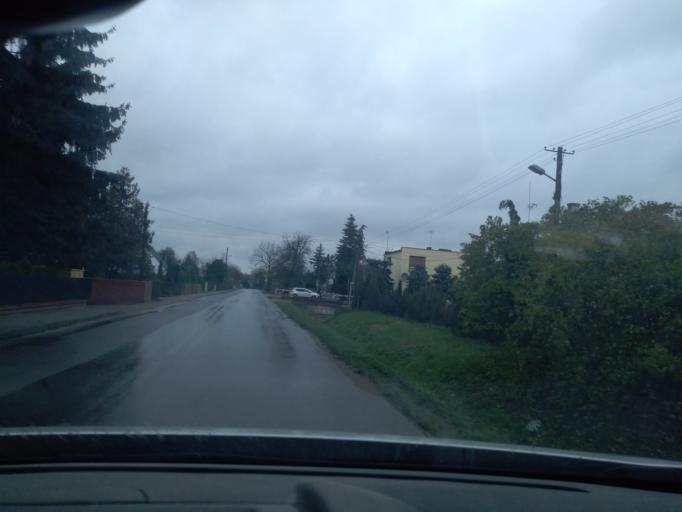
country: PL
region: Greater Poland Voivodeship
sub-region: Powiat obornicki
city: Oborniki
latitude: 52.6571
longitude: 16.8416
